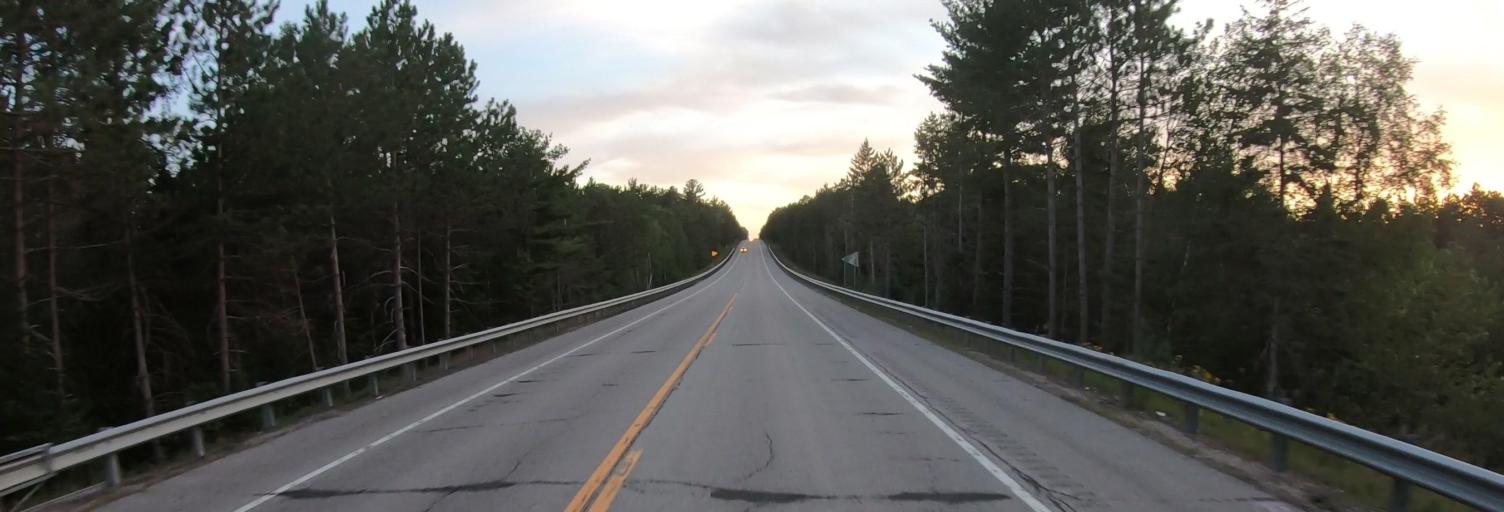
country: US
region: Minnesota
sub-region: Saint Louis County
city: Aurora
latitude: 47.7945
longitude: -92.3406
